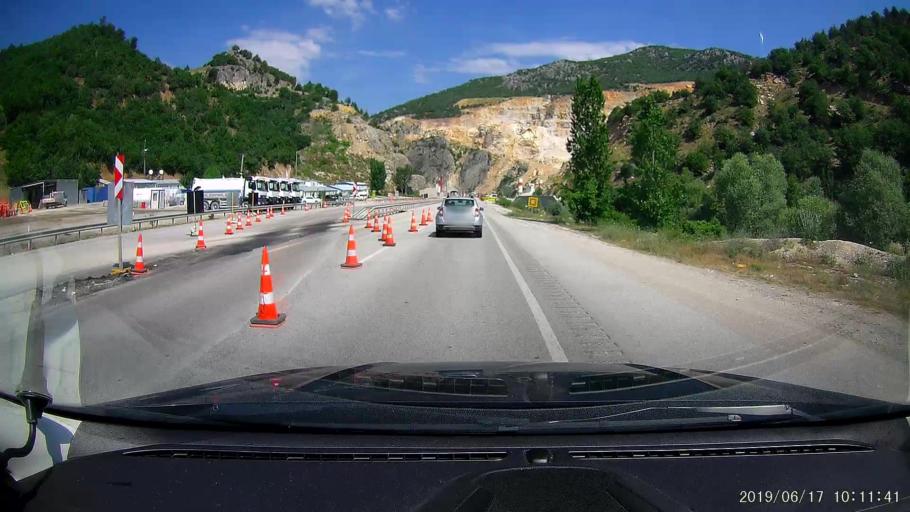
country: TR
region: Amasya
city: Saraycik
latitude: 40.9728
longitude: 35.0833
